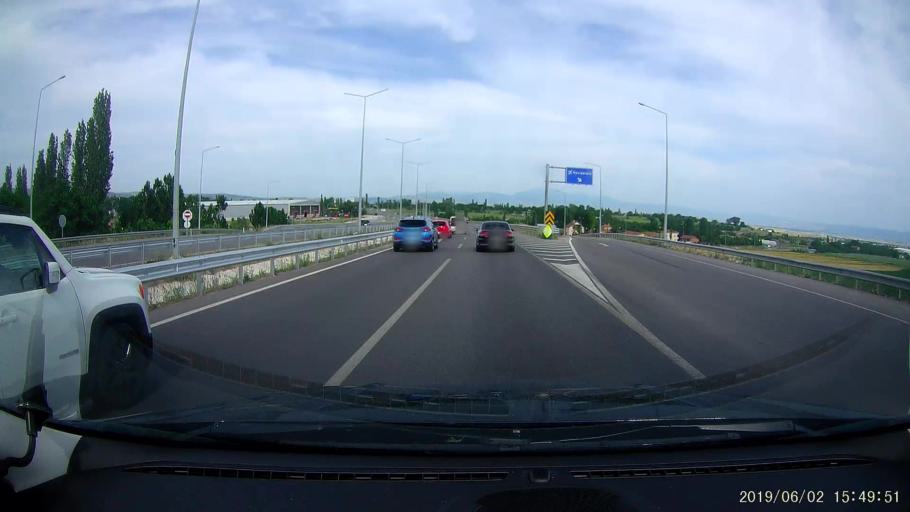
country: TR
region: Amasya
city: Merzifon
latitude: 40.8569
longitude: 35.4699
